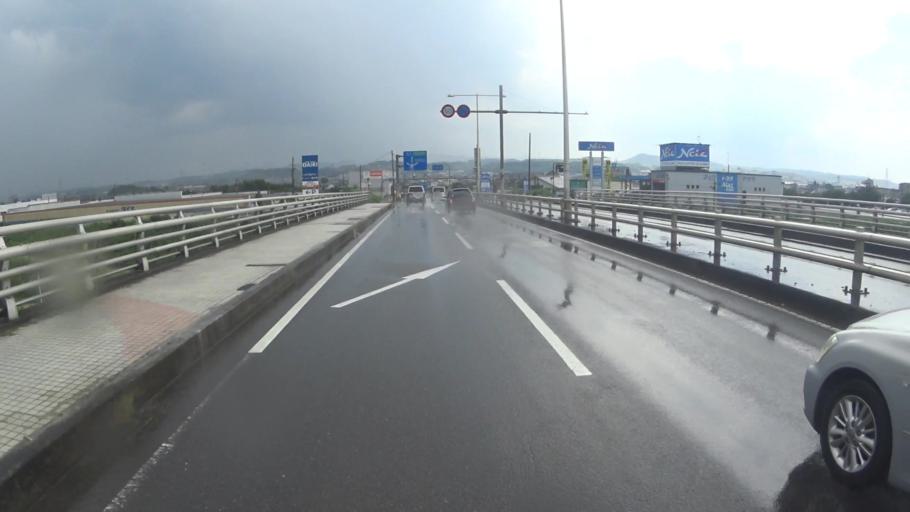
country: JP
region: Kyoto
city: Tanabe
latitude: 34.8199
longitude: 135.7908
